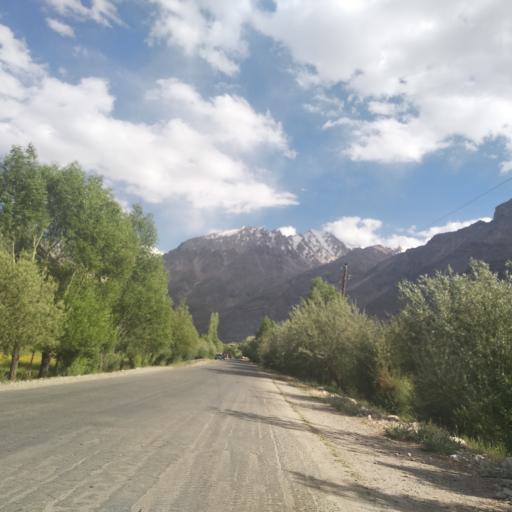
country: TJ
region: Gorno-Badakhshan
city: Roshtqal'a
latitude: 37.7264
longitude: 72.1603
